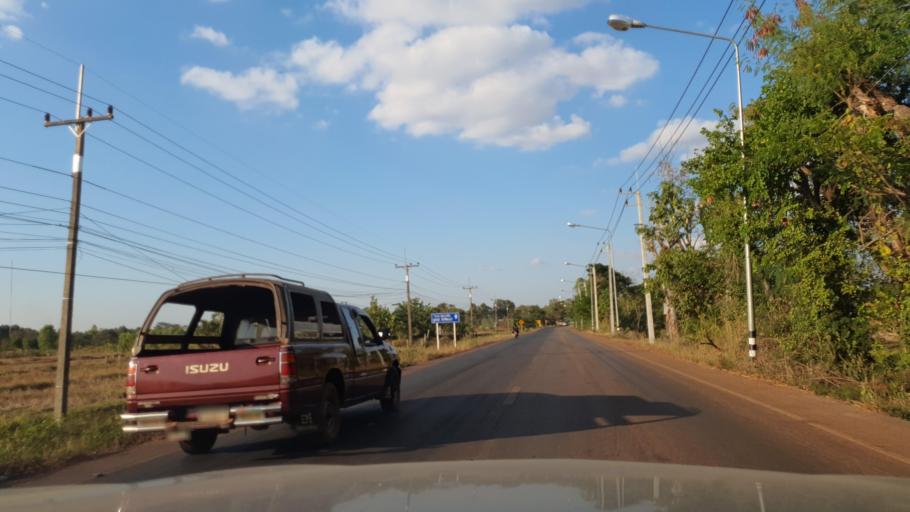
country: TH
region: Sakon Nakhon
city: Phon Na Kaeo
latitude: 17.2667
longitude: 104.1915
